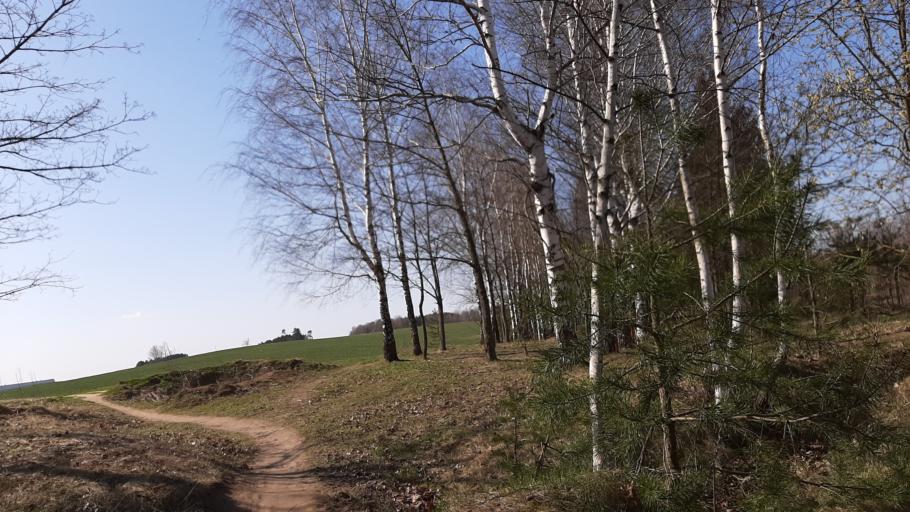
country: BY
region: Minsk
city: Bal'shavik
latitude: 53.9589
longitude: 27.5705
